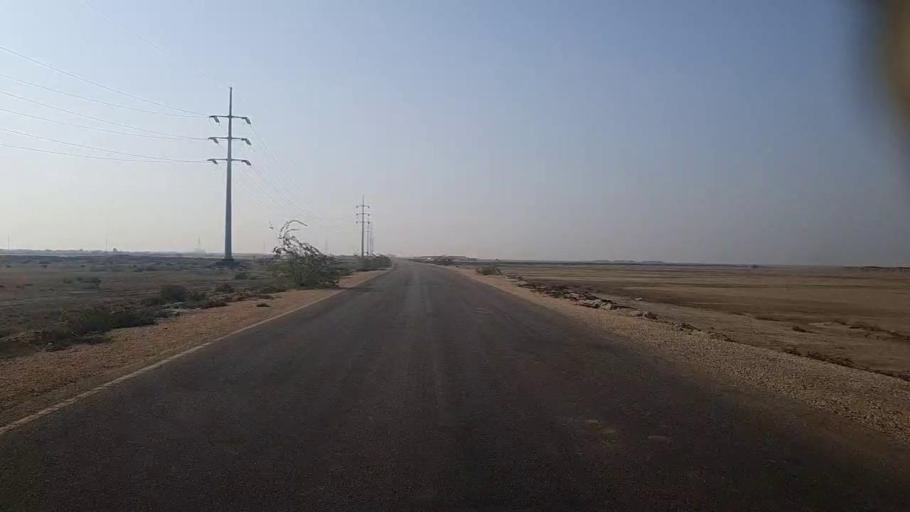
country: PK
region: Sindh
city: Gharo
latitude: 24.7367
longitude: 67.5347
